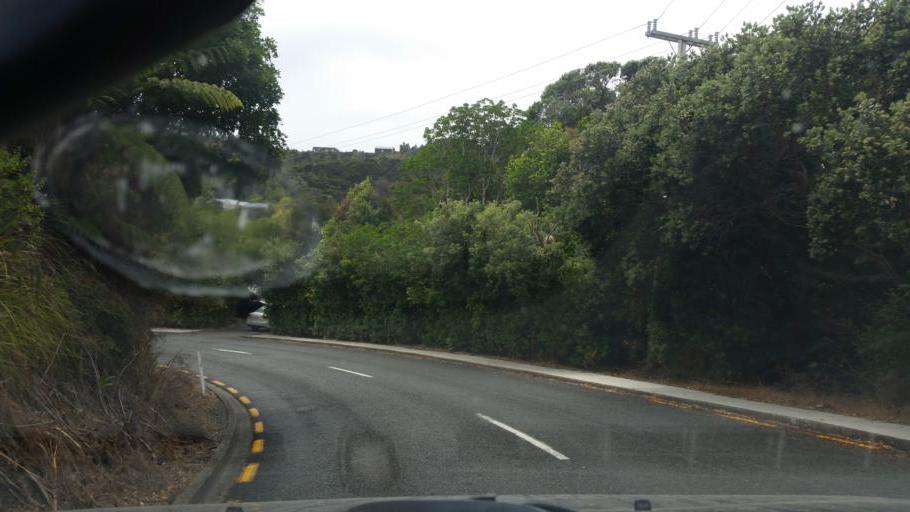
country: NZ
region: Auckland
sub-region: Auckland
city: Wellsford
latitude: -36.0831
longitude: 174.5890
